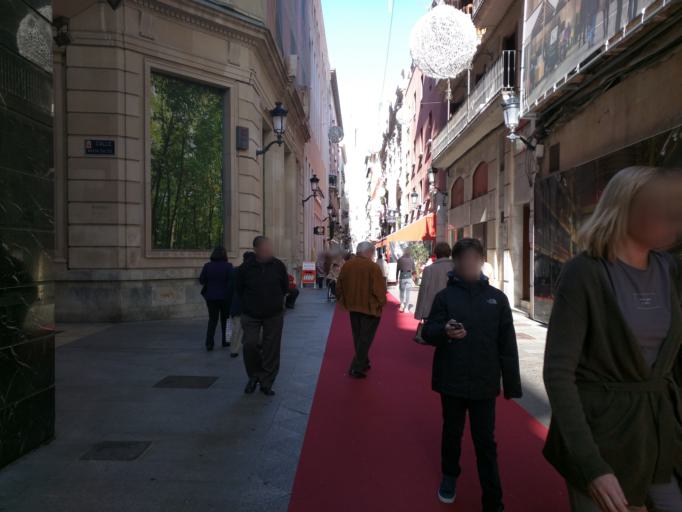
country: ES
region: Murcia
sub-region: Murcia
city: Murcia
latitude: 37.9849
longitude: -1.1290
